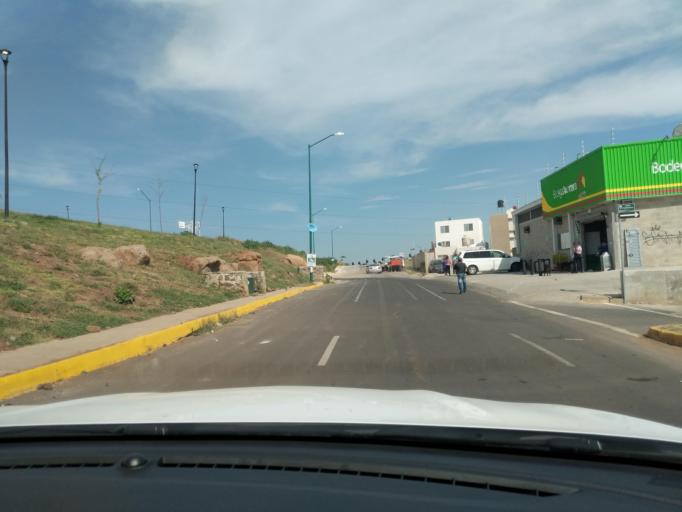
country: MX
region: Jalisco
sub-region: El Salto
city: El Muey
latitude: 20.5207
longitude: -103.2212
